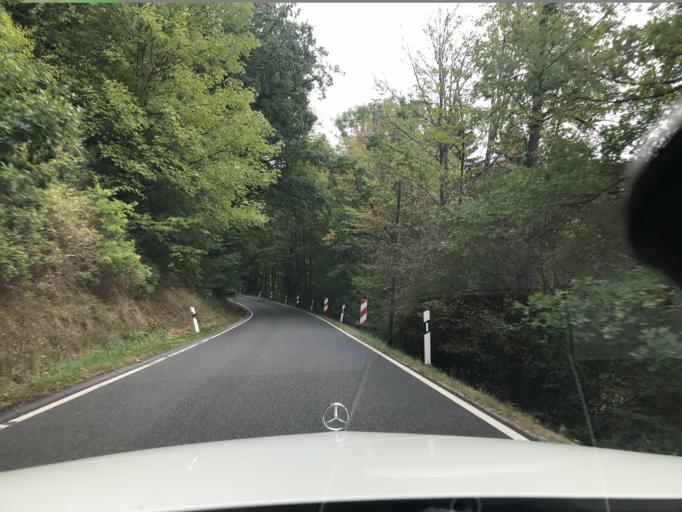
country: DE
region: Hesse
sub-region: Regierungsbezirk Kassel
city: Helsa
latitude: 51.2475
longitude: 9.6883
